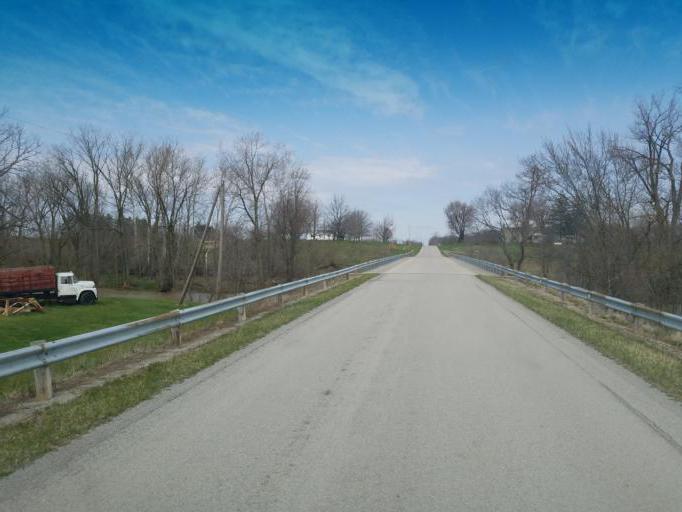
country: US
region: Ohio
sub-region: Wyandot County
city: Upper Sandusky
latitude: 40.8498
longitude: -83.2561
